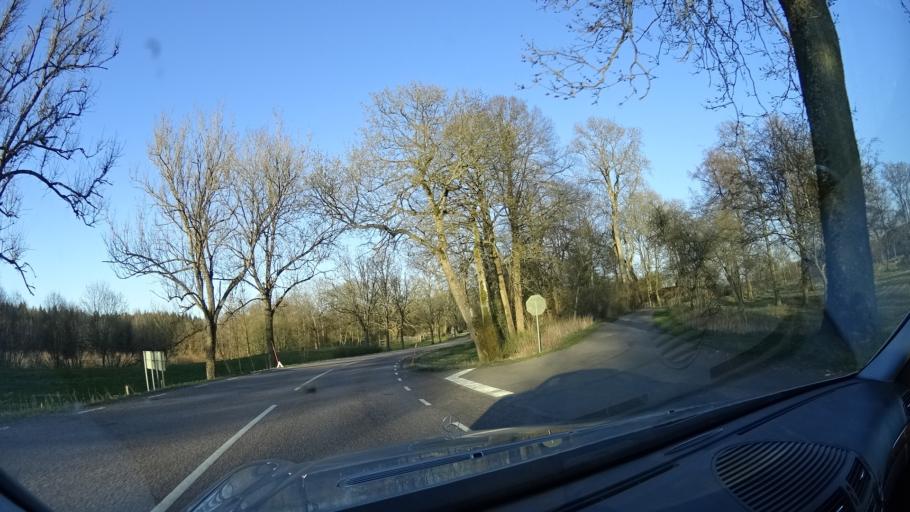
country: SE
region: Skane
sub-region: Svalovs Kommun
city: Kagerod
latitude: 55.9808
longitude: 13.1350
